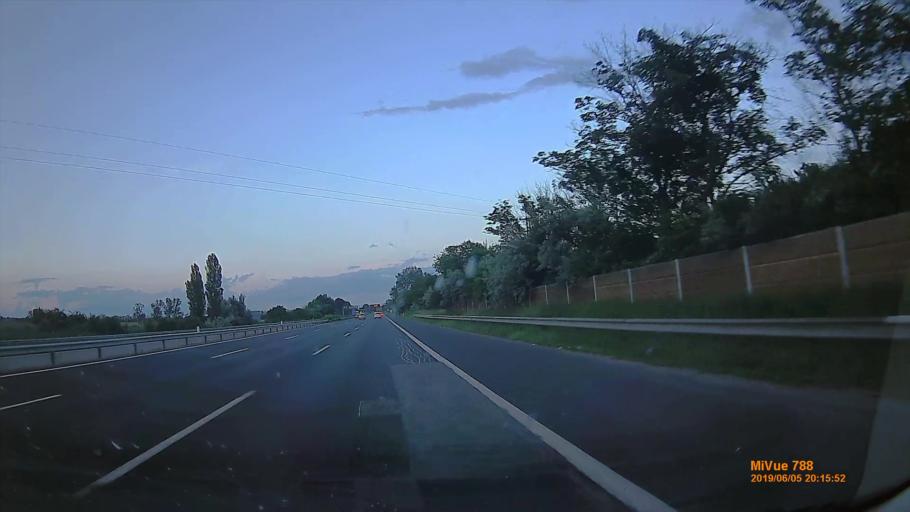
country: HU
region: Fejer
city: Velence
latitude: 47.2448
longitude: 18.6419
